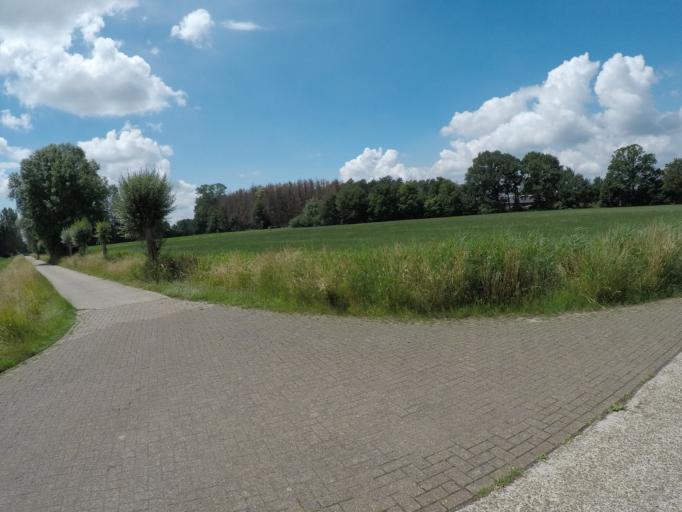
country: BE
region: Flanders
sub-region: Provincie Antwerpen
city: Vosselaar
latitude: 51.2694
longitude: 4.8863
